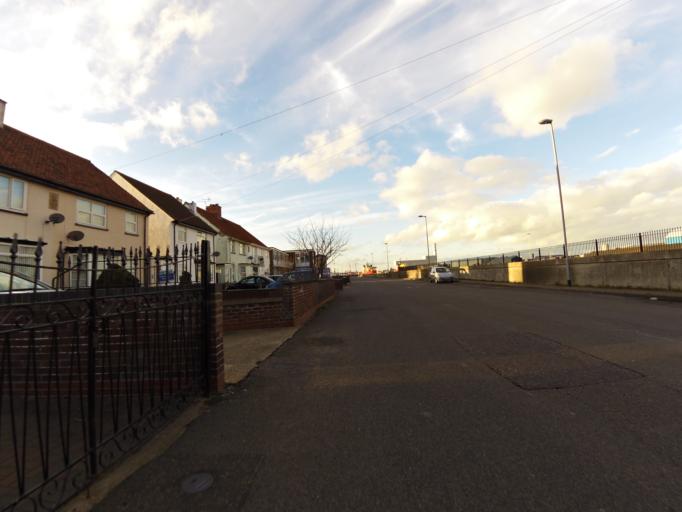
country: GB
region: England
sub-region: Norfolk
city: Gorleston-on-Sea
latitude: 52.5760
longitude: 1.7318
